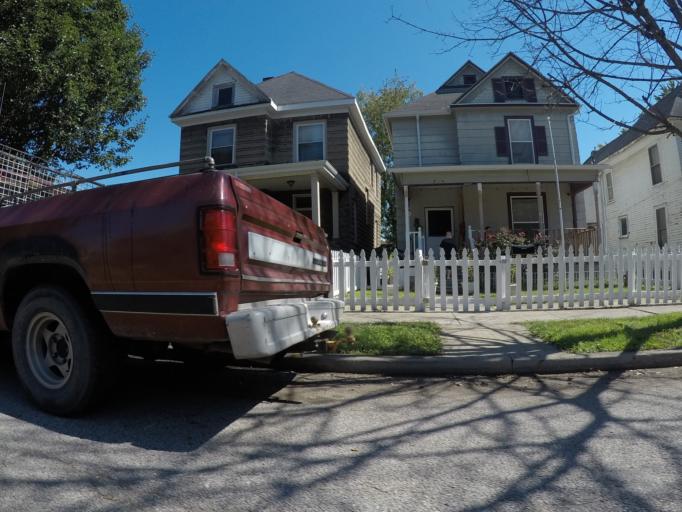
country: US
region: West Virginia
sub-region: Cabell County
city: Huntington
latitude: 38.4265
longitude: -82.3894
